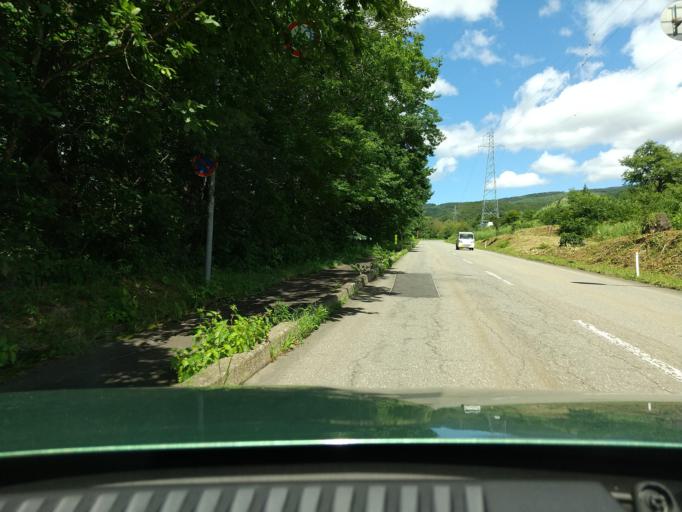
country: JP
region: Iwate
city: Shizukuishi
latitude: 39.7646
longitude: 140.7473
